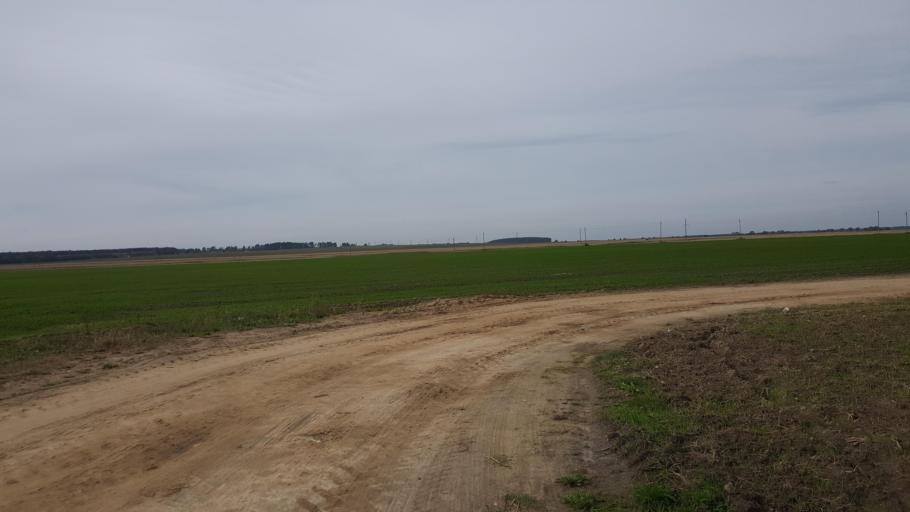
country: BY
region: Brest
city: Kamyanyets
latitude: 52.4102
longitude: 23.8906
